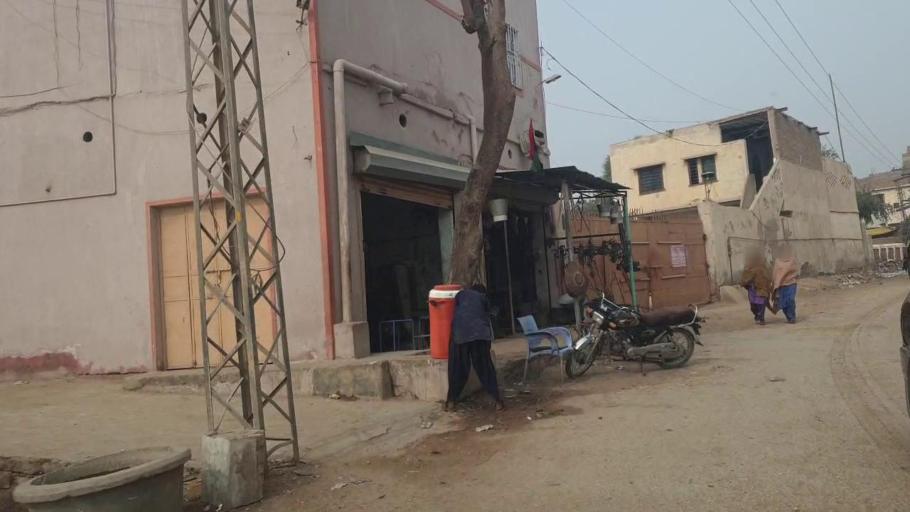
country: PK
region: Sindh
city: Tando Adam
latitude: 25.7549
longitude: 68.6656
